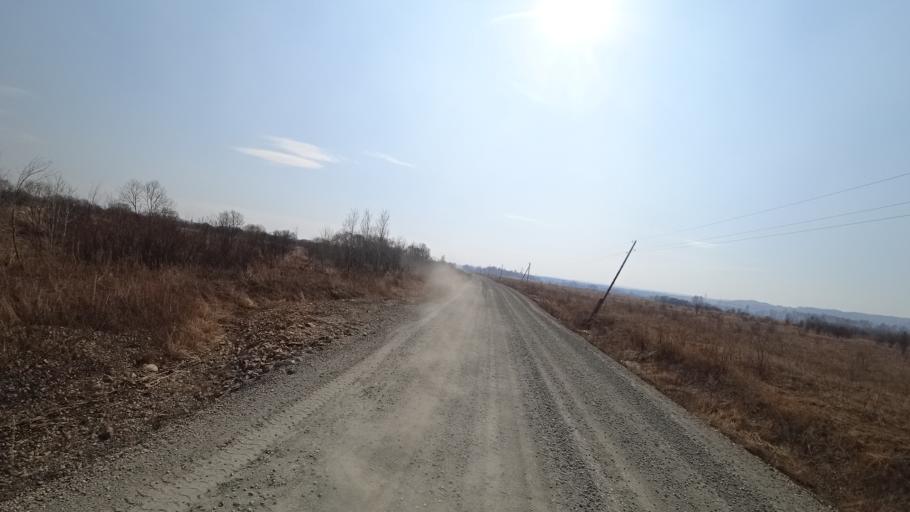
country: RU
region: Amur
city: Novobureyskiy
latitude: 49.8108
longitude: 129.9695
